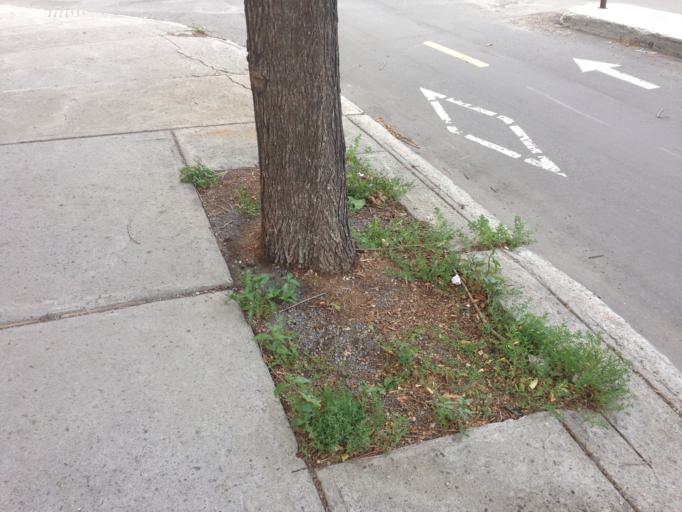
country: CA
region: Quebec
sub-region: Monteregie
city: Longueuil
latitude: 45.5224
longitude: -73.5491
